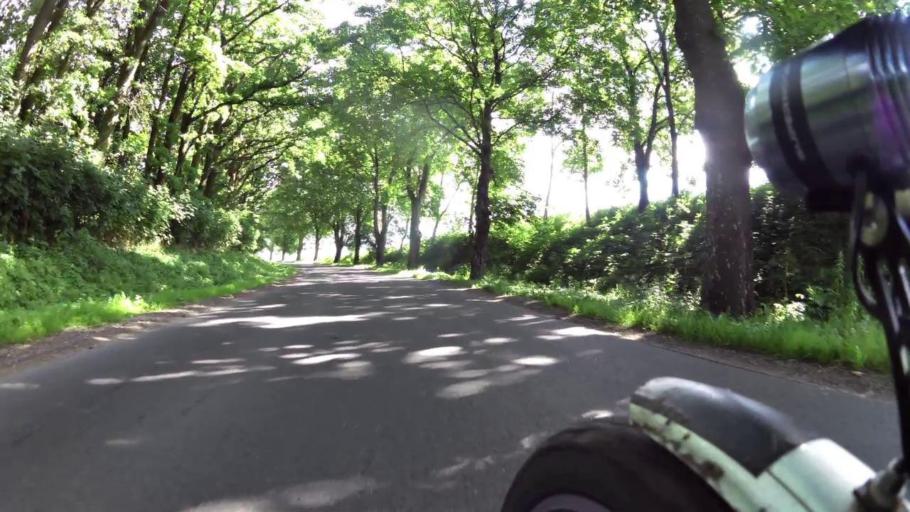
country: PL
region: West Pomeranian Voivodeship
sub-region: Powiat swidwinski
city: Rabino
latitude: 53.7833
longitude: 15.8998
